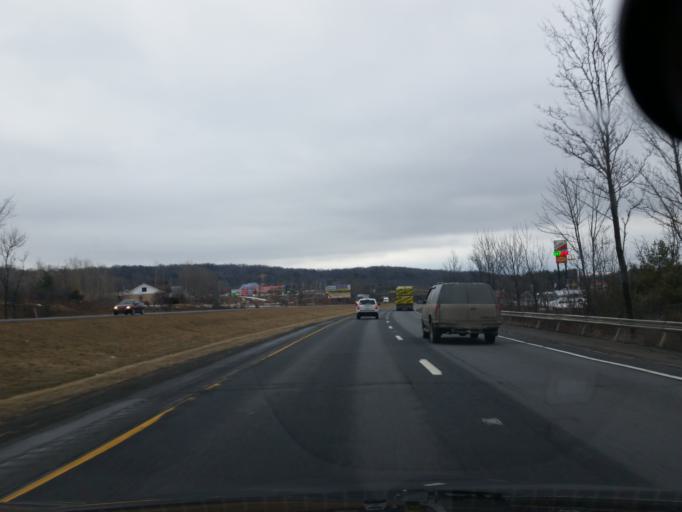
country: US
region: Pennsylvania
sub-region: Susquehanna County
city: Susquehanna
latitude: 41.8286
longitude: -75.6802
